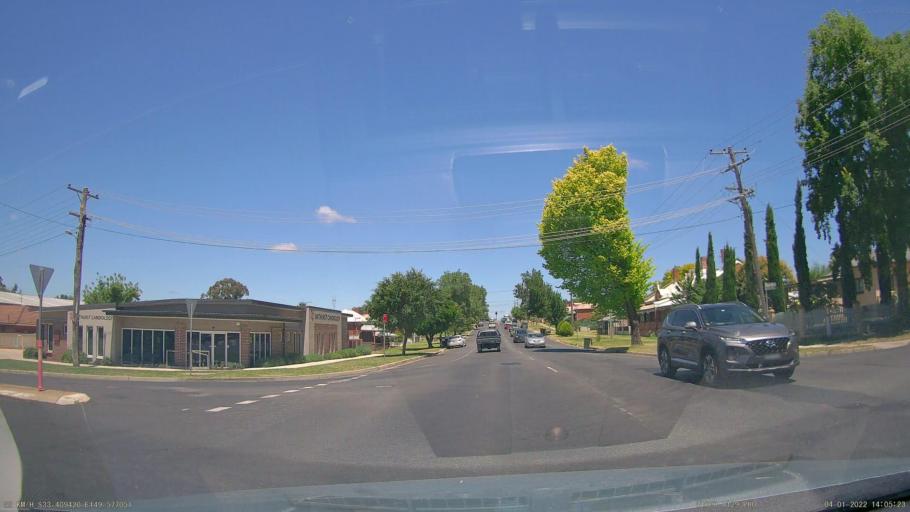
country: AU
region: New South Wales
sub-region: Bathurst Regional
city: Bathurst
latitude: -33.4096
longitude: 149.5772
